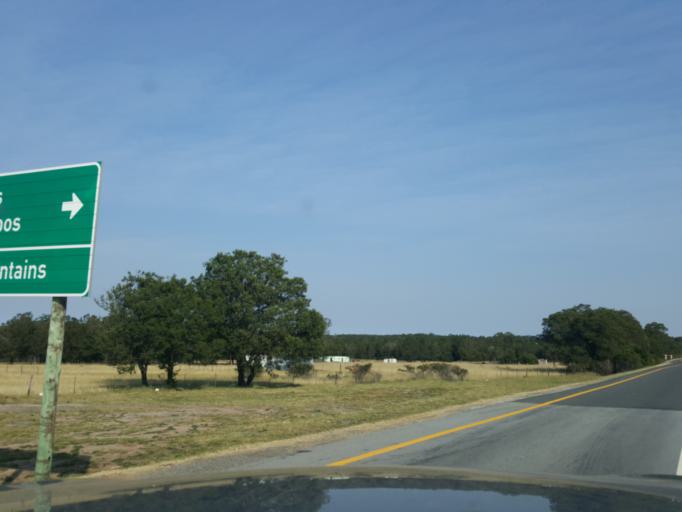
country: ZA
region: Eastern Cape
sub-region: Cacadu District Municipality
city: Grahamstown
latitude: -33.4316
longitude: 26.3223
